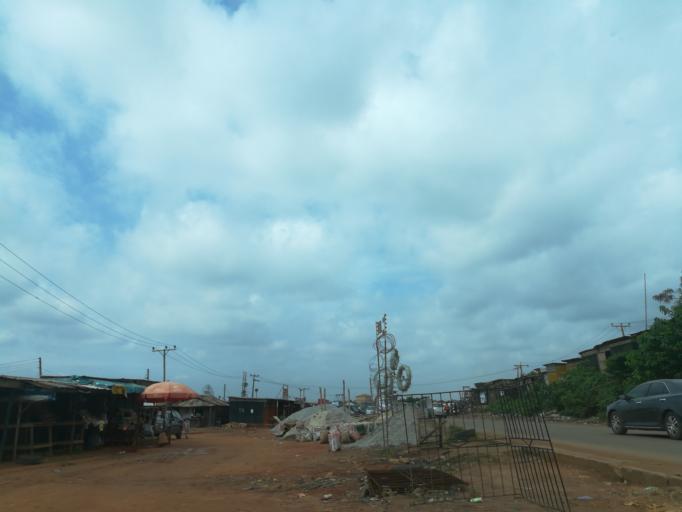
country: NG
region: Lagos
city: Ikorodu
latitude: 6.6517
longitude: 3.5769
